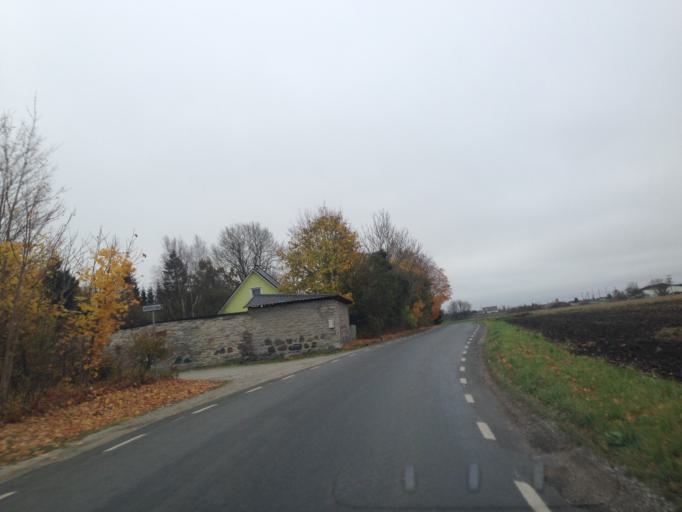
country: EE
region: Harju
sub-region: Saue linn
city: Saue
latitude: 59.3549
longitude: 24.5576
